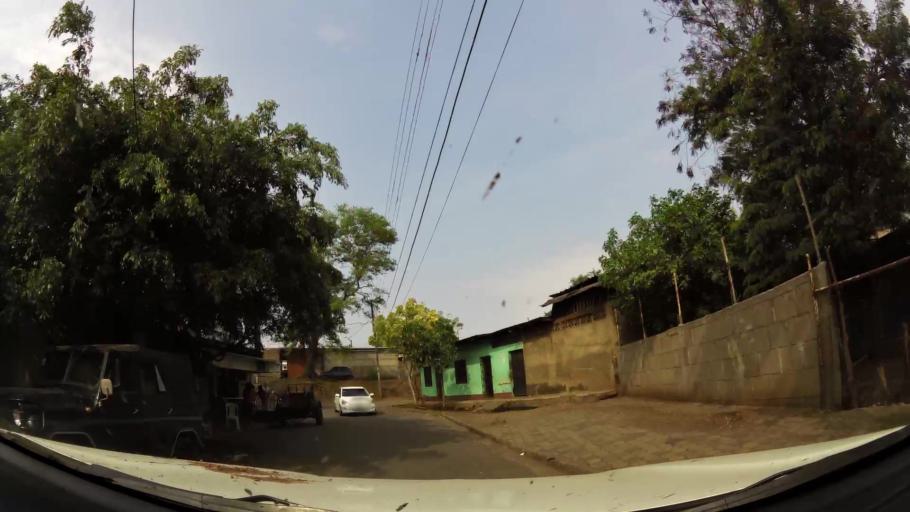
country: NI
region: Masaya
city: Masaya
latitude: 11.9718
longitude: -86.0879
